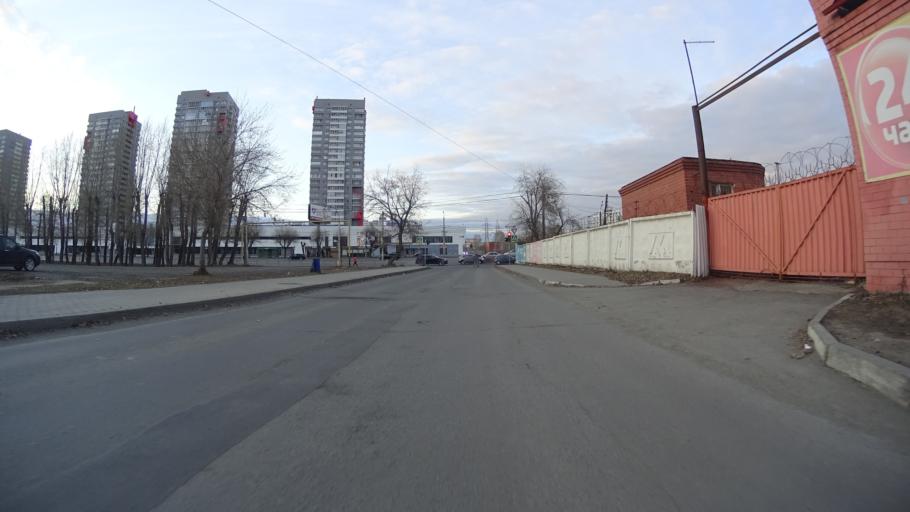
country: RU
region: Chelyabinsk
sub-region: Gorod Chelyabinsk
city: Chelyabinsk
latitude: 55.1700
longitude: 61.3703
